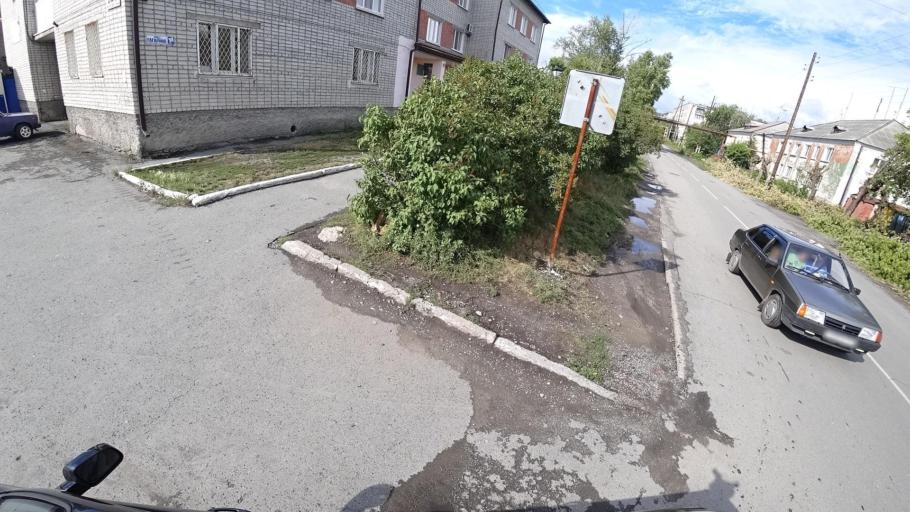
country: RU
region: Sverdlovsk
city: Kamyshlov
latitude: 56.8426
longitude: 62.7110
